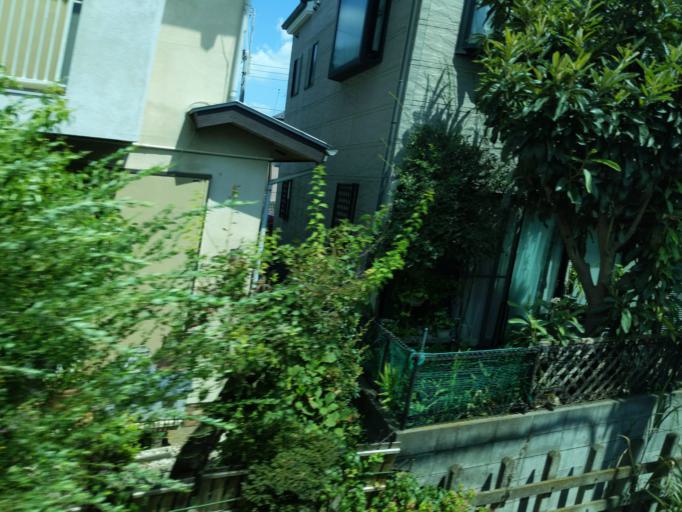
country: JP
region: Tokyo
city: Chofugaoka
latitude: 35.6296
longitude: 139.5532
